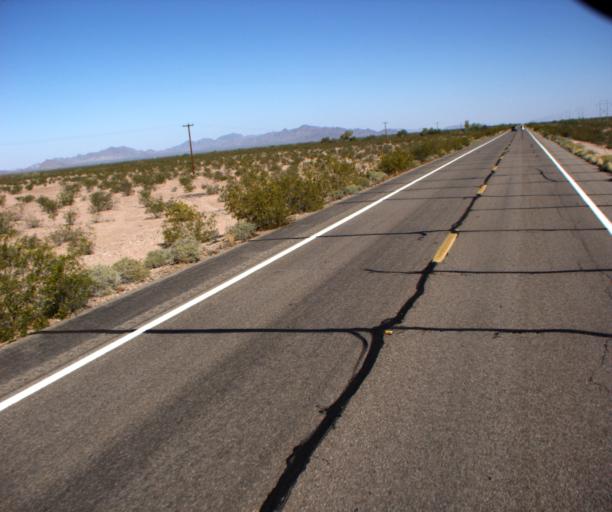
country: US
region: Arizona
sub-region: La Paz County
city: Quartzsite
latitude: 33.3457
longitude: -114.2170
